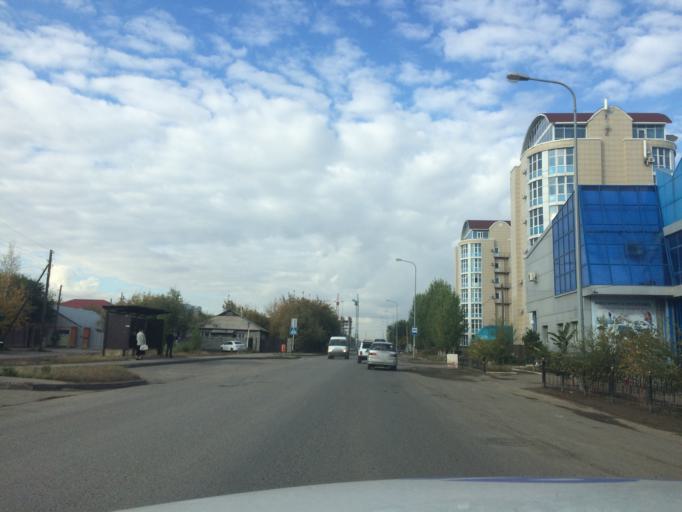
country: KZ
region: Astana Qalasy
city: Astana
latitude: 51.1807
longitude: 71.4001
